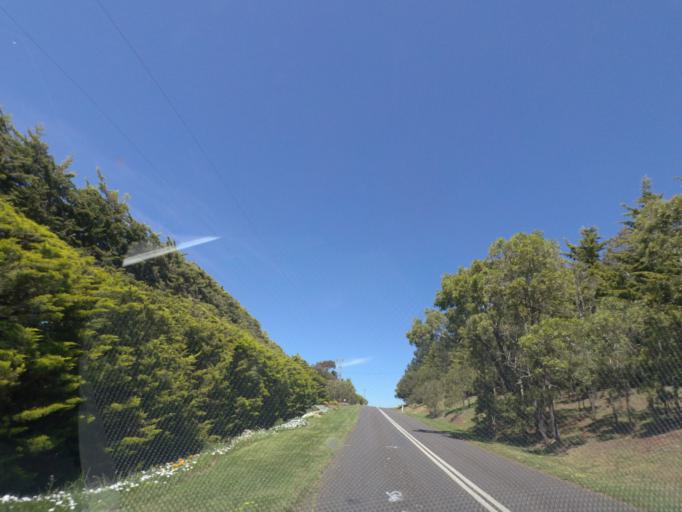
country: AU
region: Victoria
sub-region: Hume
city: Sunbury
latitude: -37.5213
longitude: 144.5891
